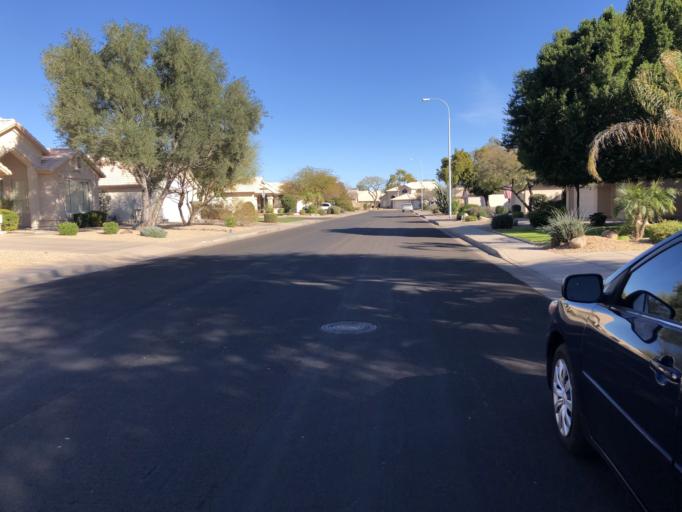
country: US
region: Arizona
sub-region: Maricopa County
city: San Carlos
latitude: 33.3139
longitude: -111.9142
